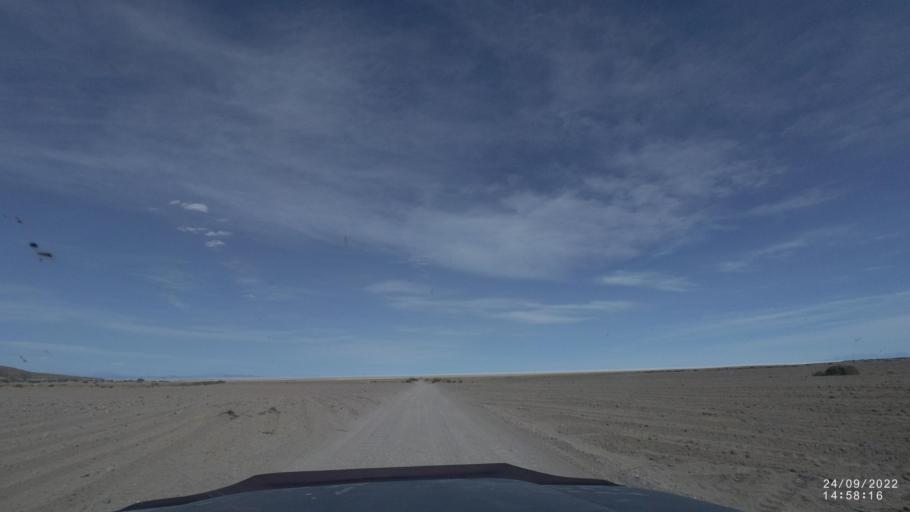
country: BO
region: Potosi
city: Colchani
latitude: -19.8599
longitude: -67.5690
